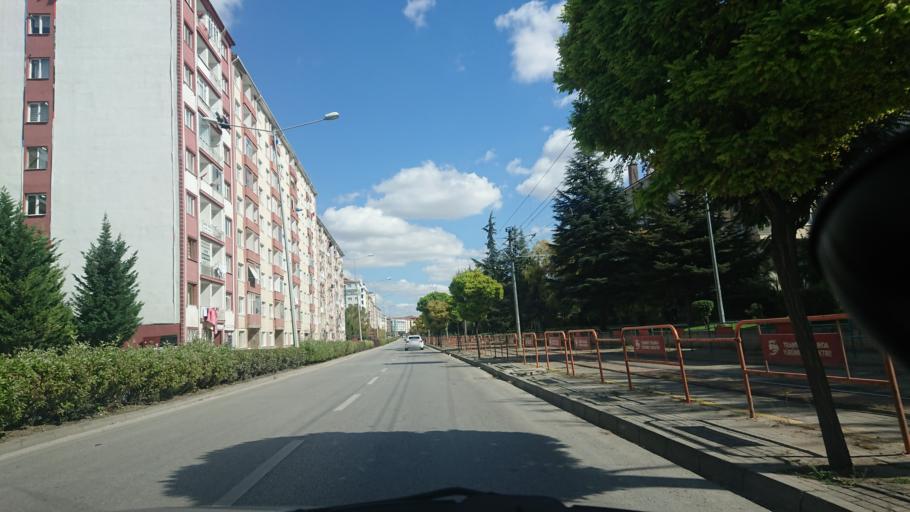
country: TR
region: Eskisehir
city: Eskisehir
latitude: 39.7676
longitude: 30.5370
